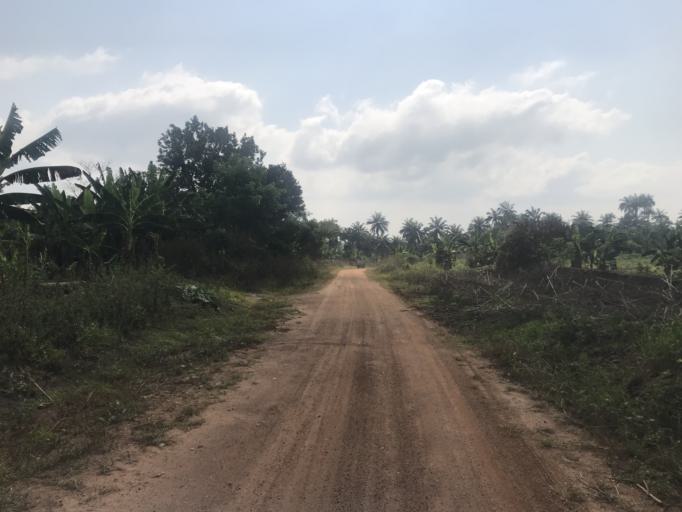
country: NG
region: Osun
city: Ikirun
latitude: 7.8513
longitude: 4.6297
